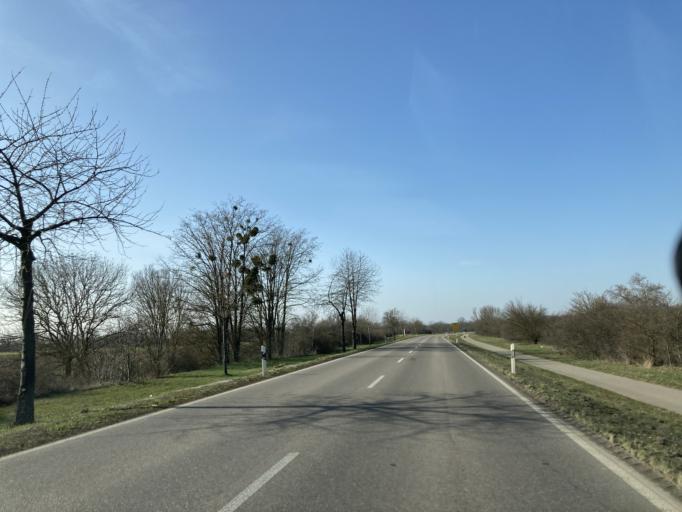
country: DE
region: Baden-Wuerttemberg
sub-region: Freiburg Region
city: Hartheim
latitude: 47.8926
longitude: 7.6029
